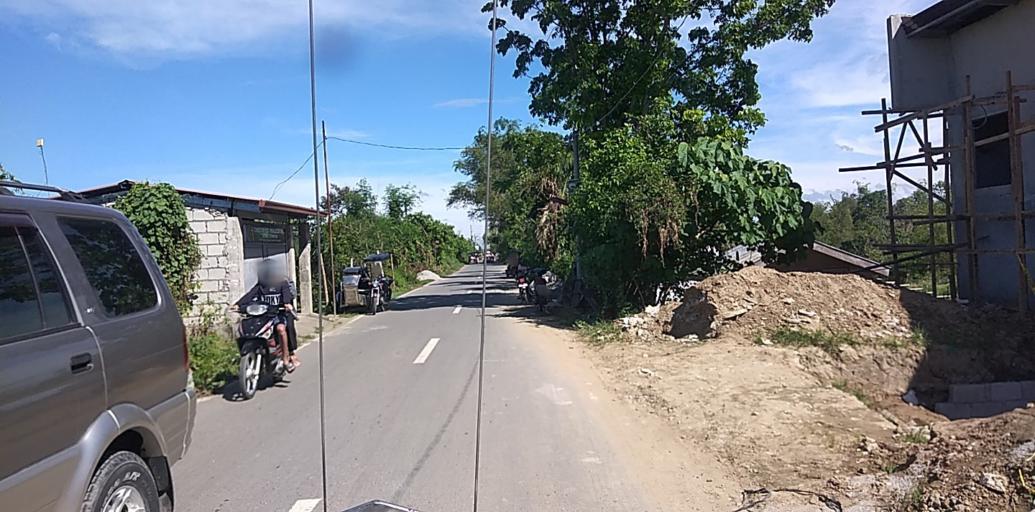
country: PH
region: Central Luzon
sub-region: Province of Pampanga
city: Candaba
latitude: 15.1029
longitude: 120.8150
